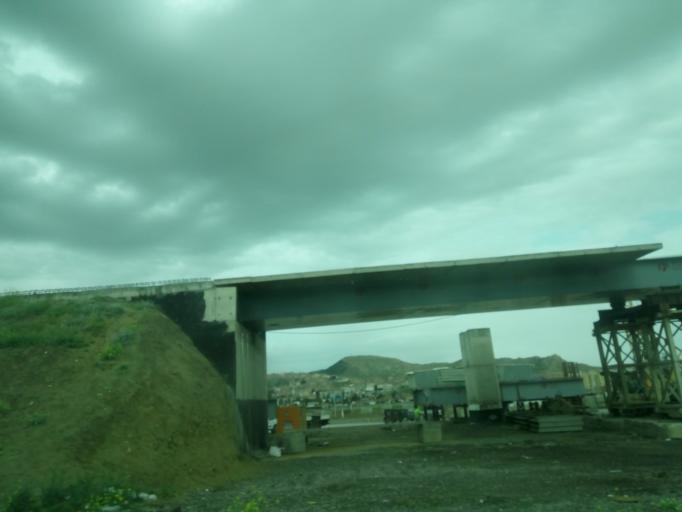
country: DZ
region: Medea
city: Ksar el Boukhari
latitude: 35.8833
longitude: 2.7356
